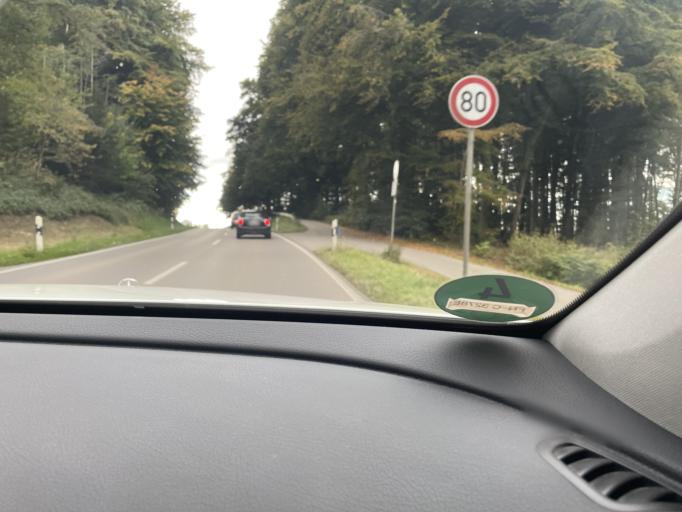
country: DE
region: Baden-Wuerttemberg
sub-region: Tuebingen Region
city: Markdorf
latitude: 47.7038
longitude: 9.4203
